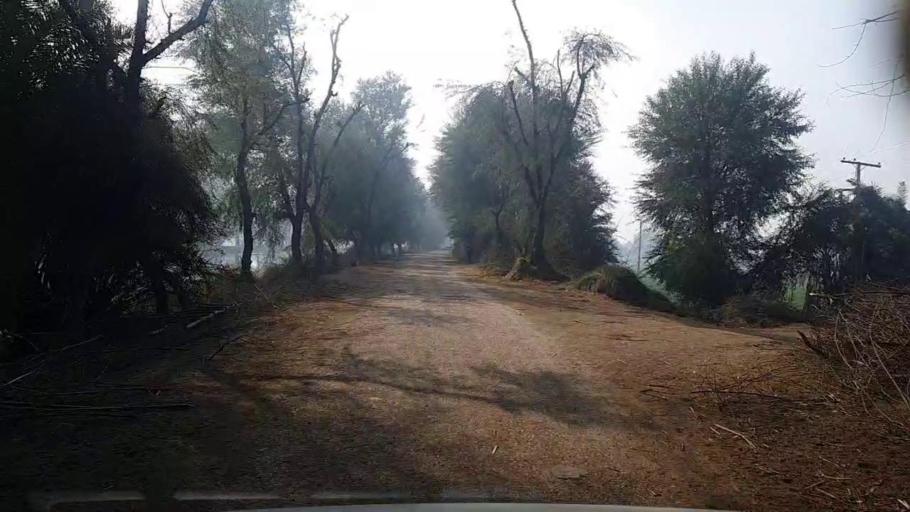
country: PK
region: Sindh
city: Khairpur
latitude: 27.9607
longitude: 69.6542
